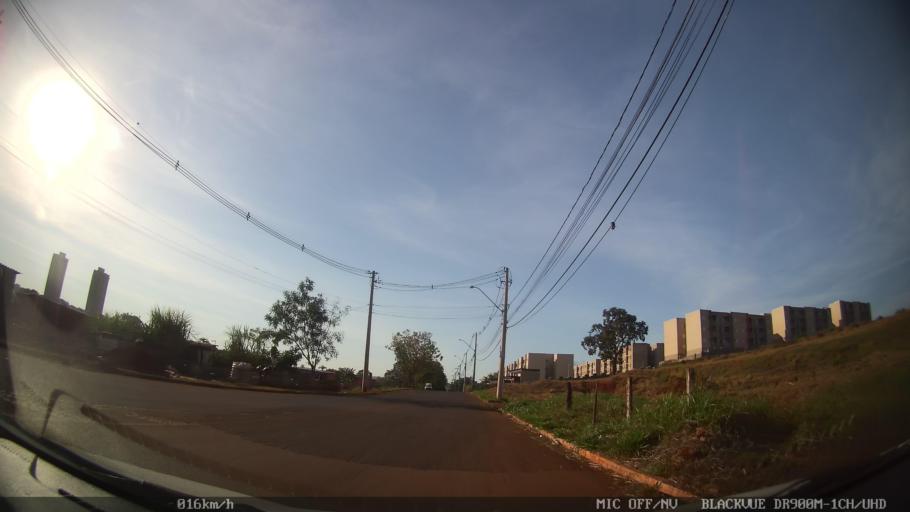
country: BR
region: Sao Paulo
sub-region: Ribeirao Preto
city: Ribeirao Preto
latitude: -21.2710
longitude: -47.8173
